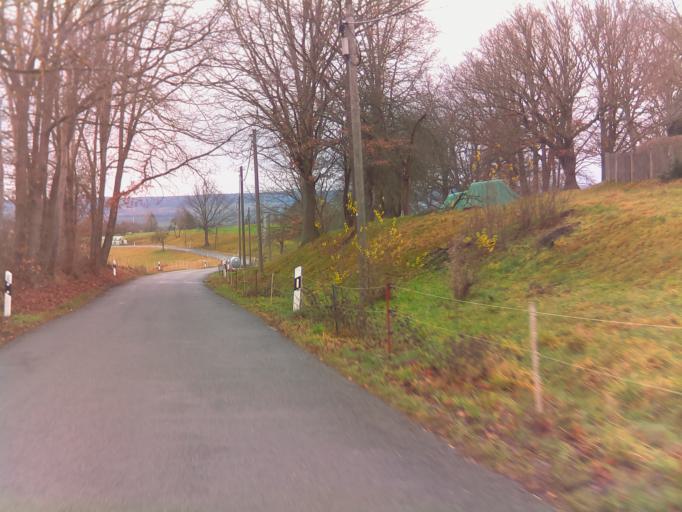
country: DE
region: Thuringia
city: Tissa
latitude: 50.8502
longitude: 11.7430
